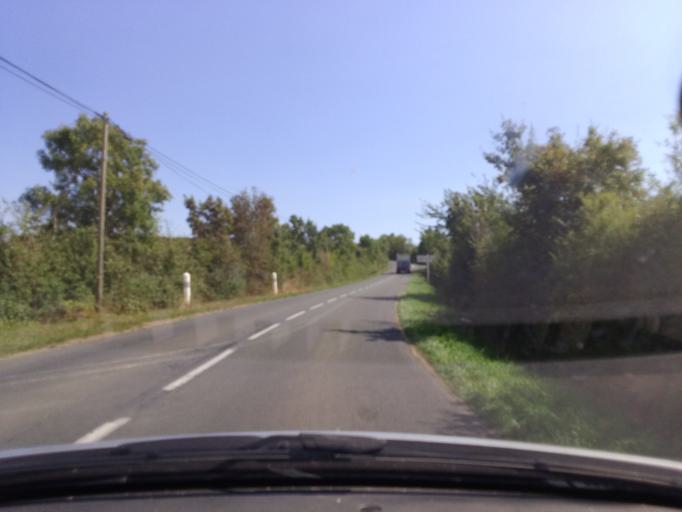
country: FR
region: Pays de la Loire
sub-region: Departement de la Vendee
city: Les Magnils-Reigniers
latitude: 46.4422
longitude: -1.2652
